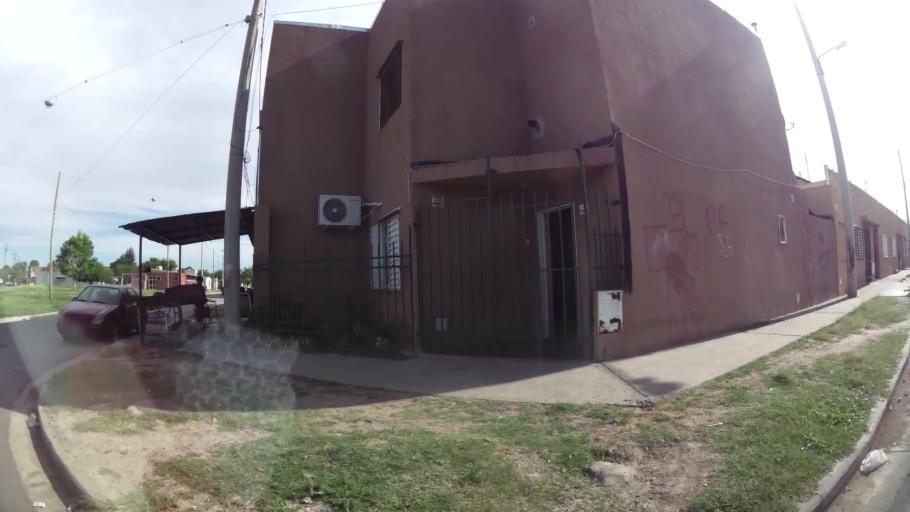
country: AR
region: Santa Fe
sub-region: Departamento de Rosario
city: Rosario
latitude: -32.9182
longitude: -60.6904
